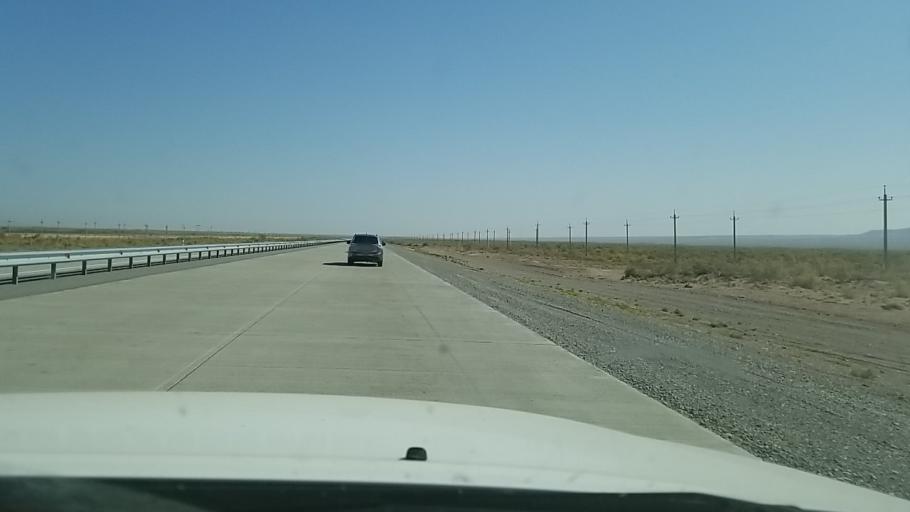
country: KZ
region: Almaty Oblysy
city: Kegen
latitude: 43.7339
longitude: 78.7956
